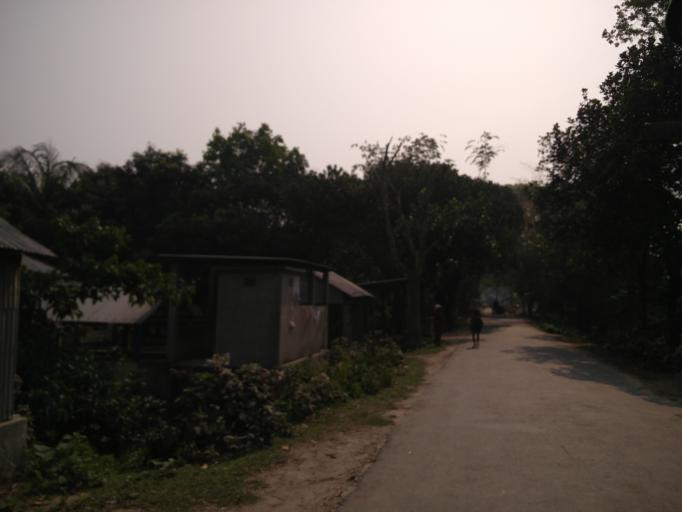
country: BD
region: Dhaka
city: Muktagacha
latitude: 24.9106
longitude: 90.1577
